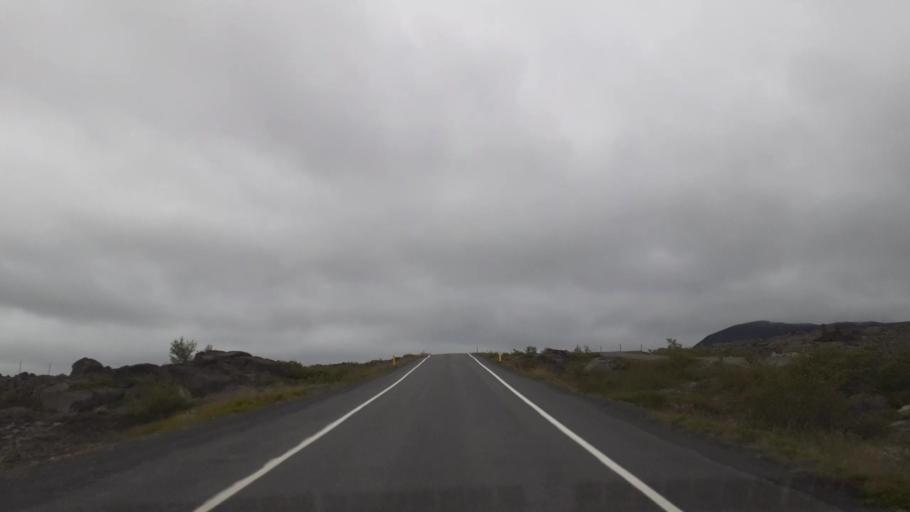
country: IS
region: Northeast
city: Husavik
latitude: 66.0337
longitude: -16.4423
